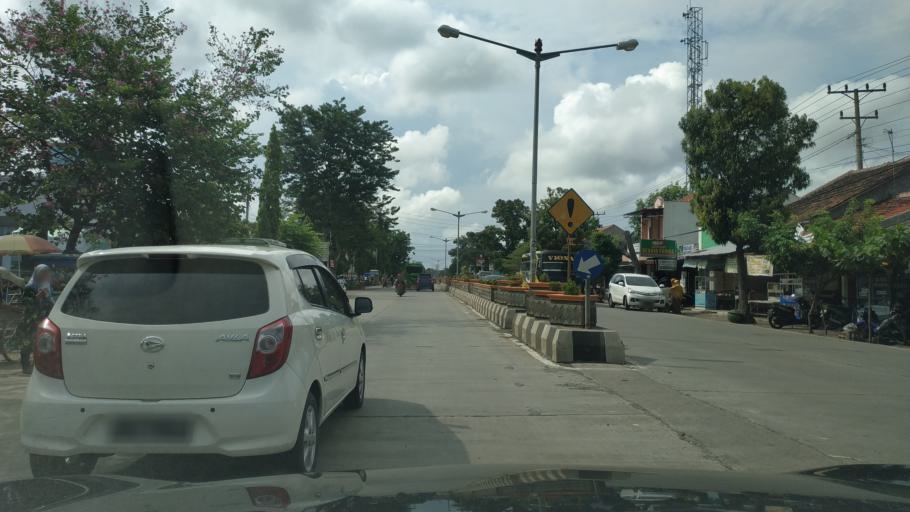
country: ID
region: Central Java
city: Pemalang
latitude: -6.9105
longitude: 109.3828
